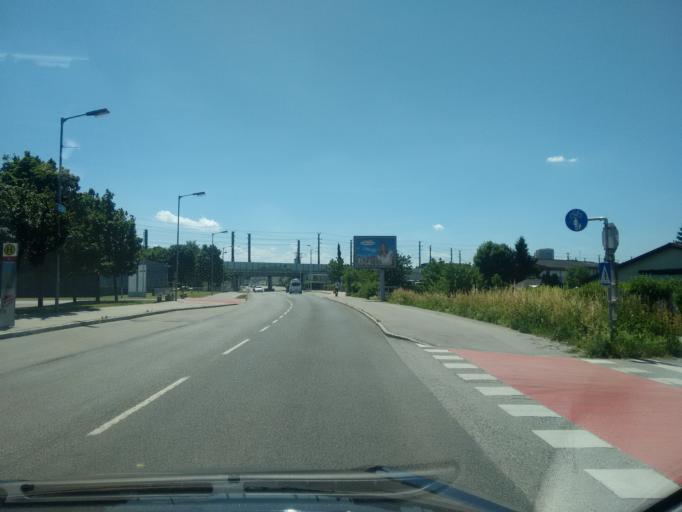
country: AT
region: Lower Austria
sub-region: Sankt Polten Stadt
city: Sankt Poelten
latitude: 48.2086
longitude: 15.6431
